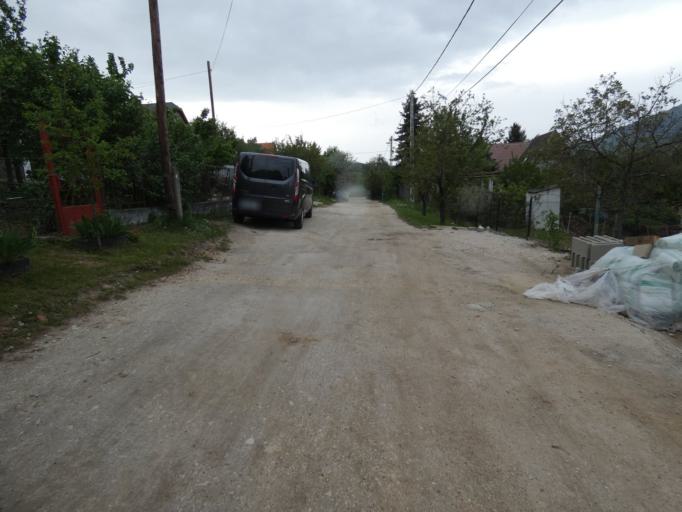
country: HU
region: Pest
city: Pilisborosjeno
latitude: 47.6027
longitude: 18.9891
